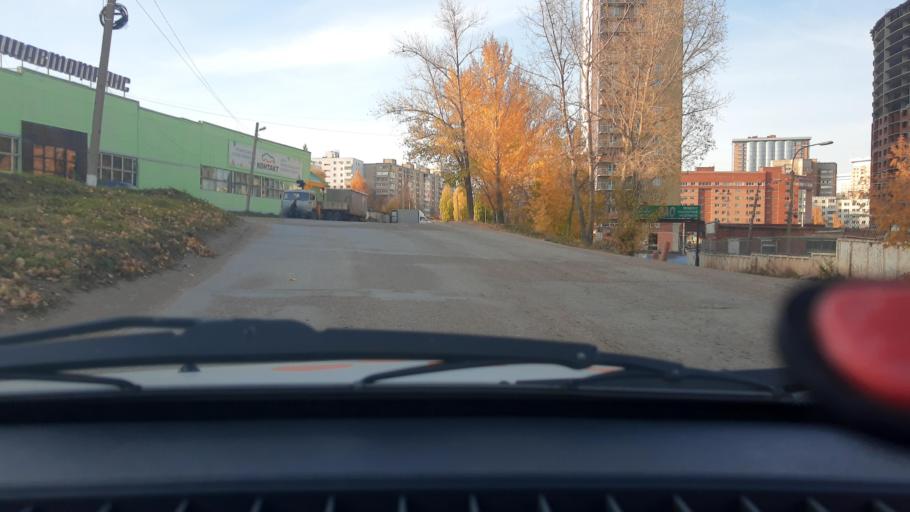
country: RU
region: Bashkortostan
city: Ufa
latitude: 54.7238
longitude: 55.9993
